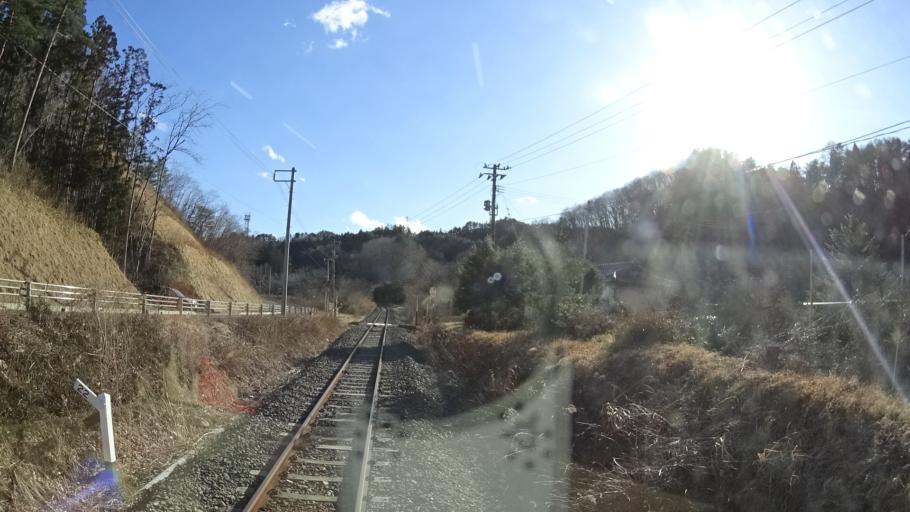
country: JP
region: Iwate
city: Miyako
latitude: 39.6082
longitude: 141.9327
